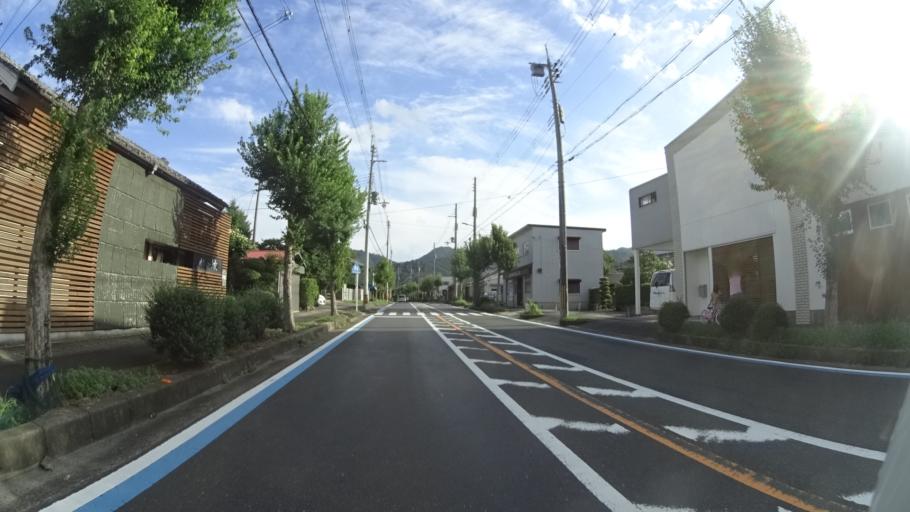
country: JP
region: Kyoto
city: Maizuru
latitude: 35.4592
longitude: 135.3970
